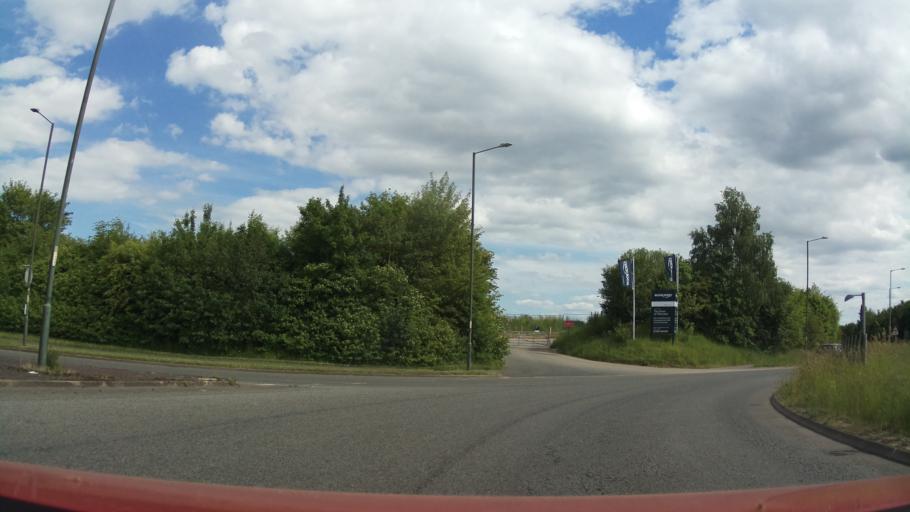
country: GB
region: England
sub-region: Worcestershire
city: Bransford
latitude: 52.1889
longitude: -2.2656
